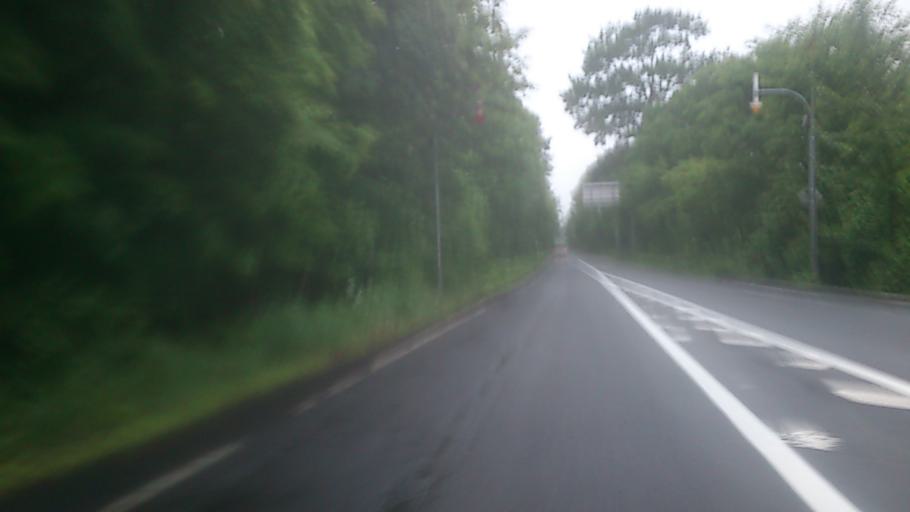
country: JP
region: Hokkaido
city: Chitose
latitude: 42.7933
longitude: 141.5036
